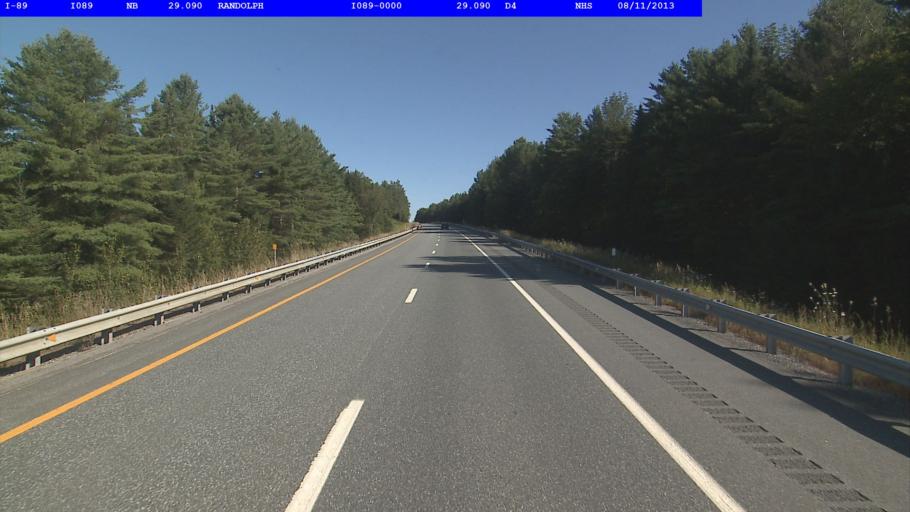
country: US
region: Vermont
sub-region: Orange County
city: Randolph
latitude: 43.9193
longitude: -72.6132
